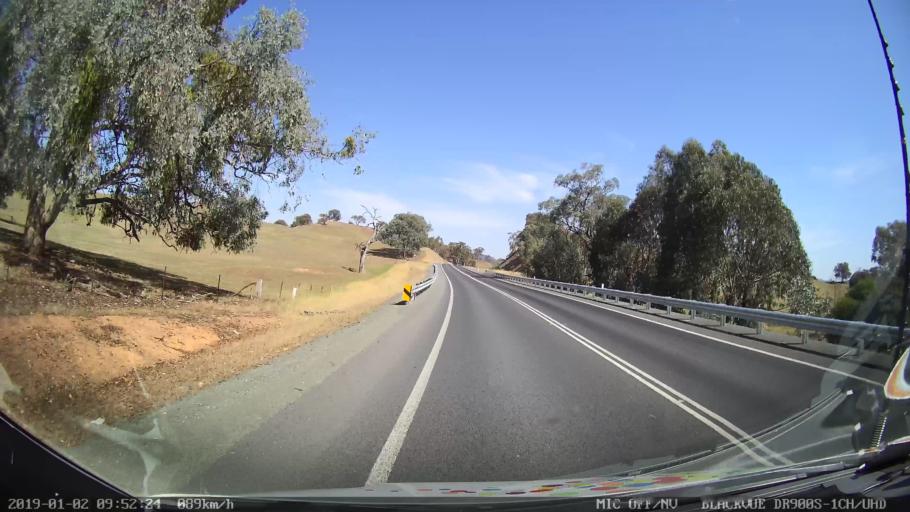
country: AU
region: New South Wales
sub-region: Tumut Shire
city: Tumut
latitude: -35.2613
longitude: 148.2067
